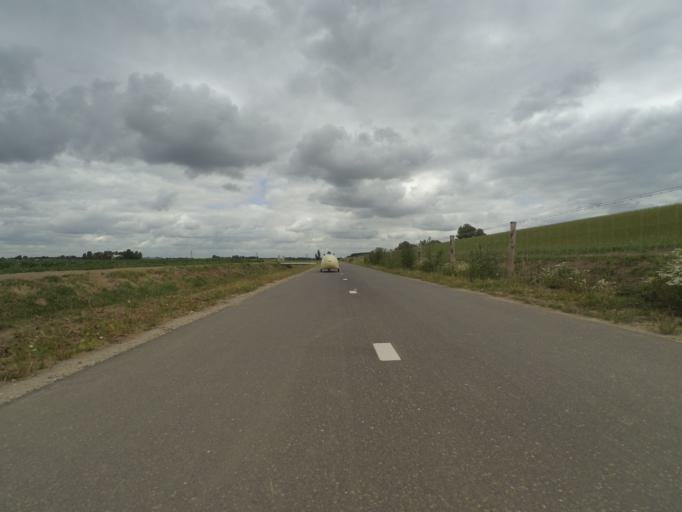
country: NL
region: South Holland
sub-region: Gemeente Dordrecht
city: Dordrecht
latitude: 51.7558
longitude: 4.6701
